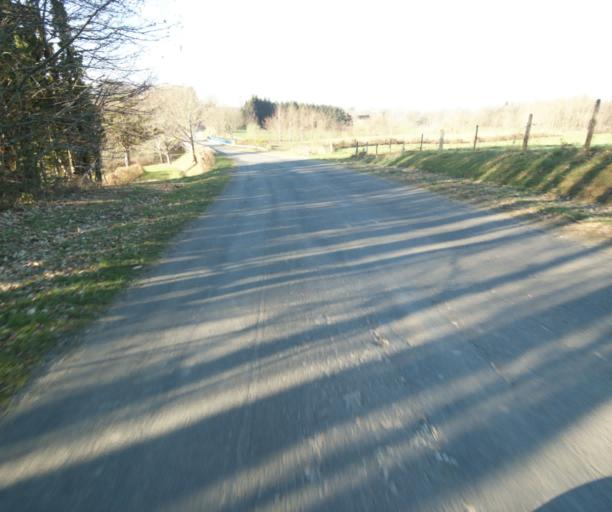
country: FR
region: Limousin
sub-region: Departement de la Correze
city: Uzerche
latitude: 45.3893
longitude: 1.5902
